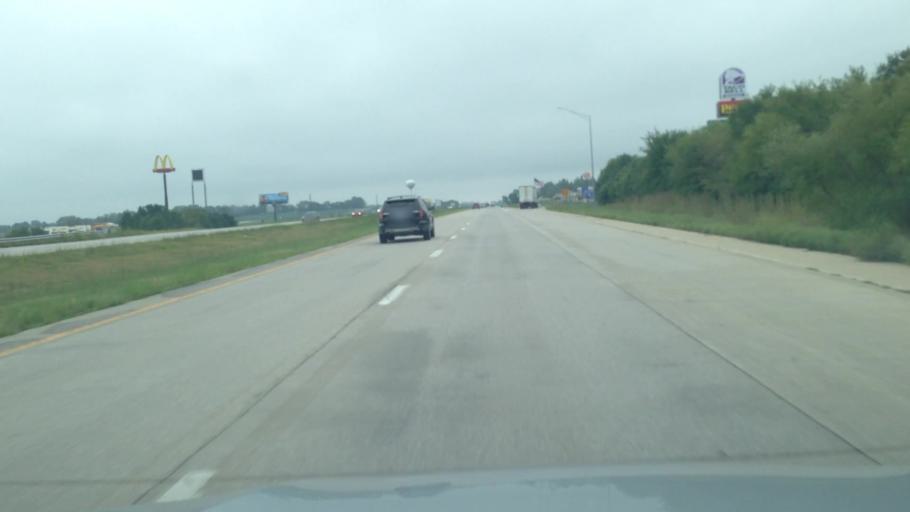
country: US
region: Missouri
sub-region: Clay County
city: Kearney
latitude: 39.3713
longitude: -94.3707
